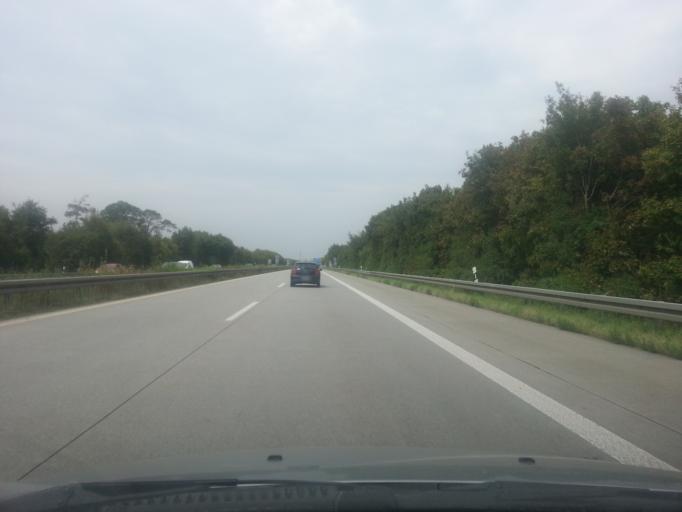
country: DE
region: Baden-Wuerttemberg
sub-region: Karlsruhe Region
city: Hockenheim
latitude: 49.3484
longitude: 8.5530
